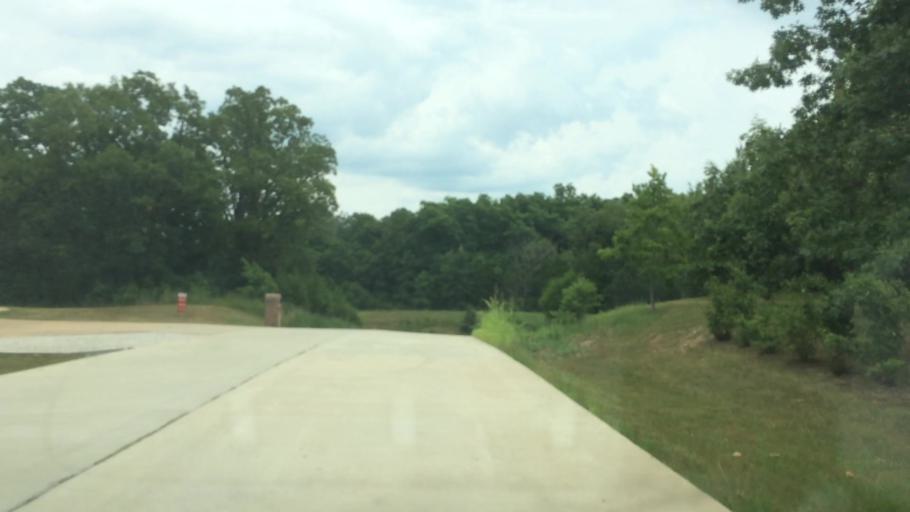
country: US
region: Missouri
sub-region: Greene County
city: Strafford
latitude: 37.2789
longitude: -93.0482
